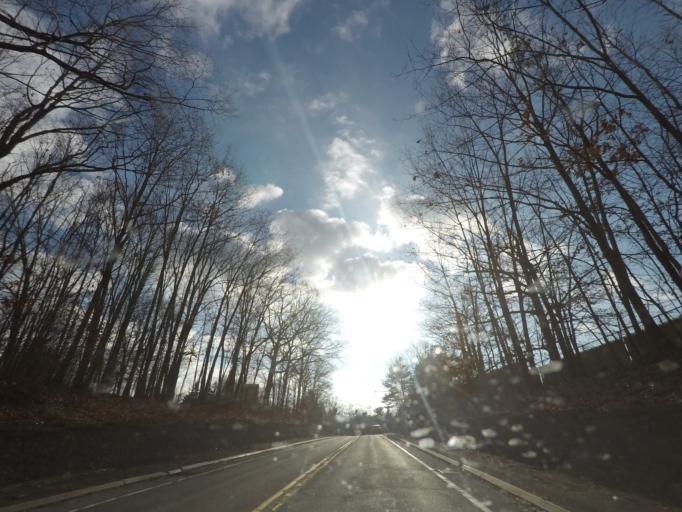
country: US
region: New York
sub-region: Albany County
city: Voorheesville
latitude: 42.6510
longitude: -73.9202
